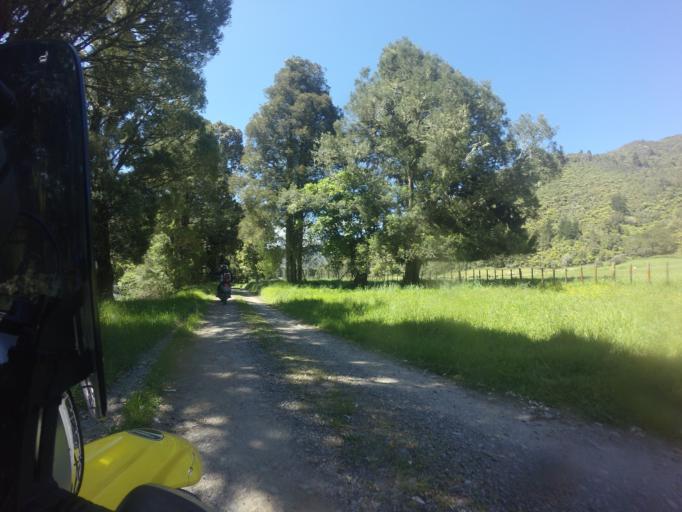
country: NZ
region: Bay of Plenty
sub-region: Opotiki District
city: Opotiki
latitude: -38.3012
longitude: 177.3346
